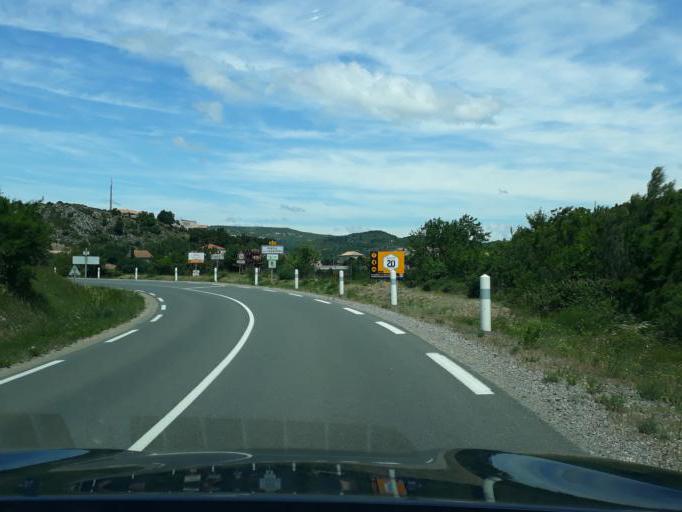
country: FR
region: Languedoc-Roussillon
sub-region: Departement de l'Aude
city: Portel-des-Corbieres
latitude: 43.0468
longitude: 2.9269
